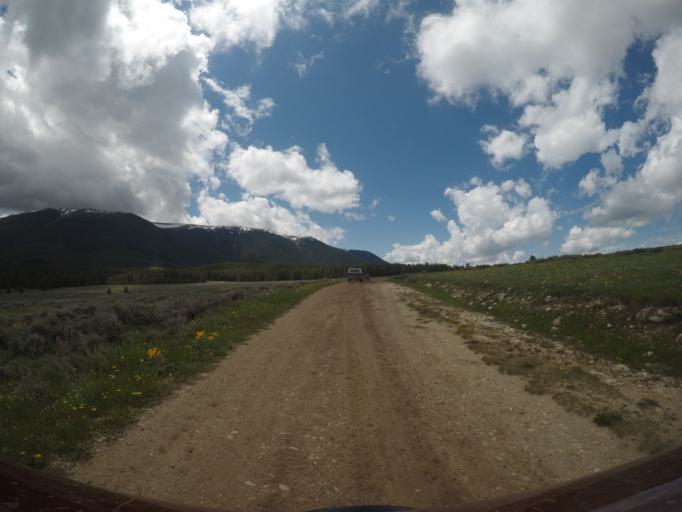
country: US
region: Wyoming
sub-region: Big Horn County
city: Lovell
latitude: 45.1791
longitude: -108.4439
